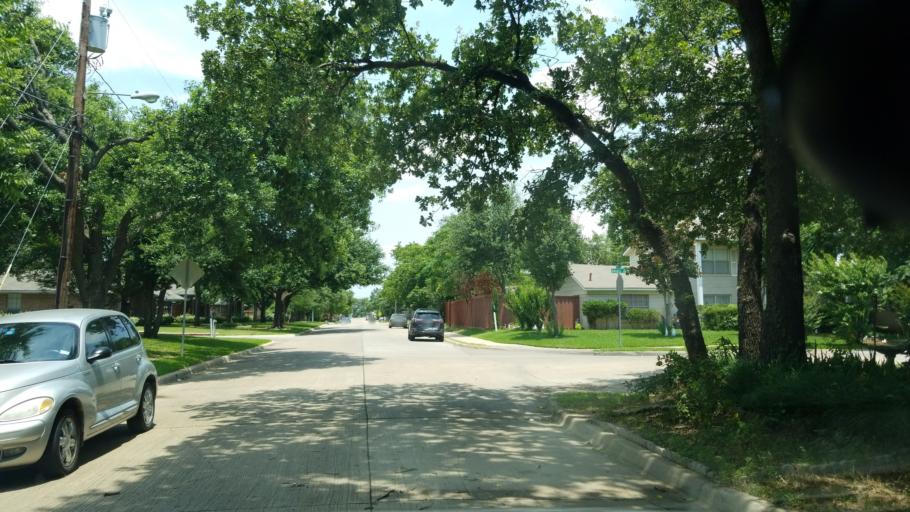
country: US
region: Texas
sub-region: Dallas County
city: Irving
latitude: 32.8410
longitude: -96.9550
